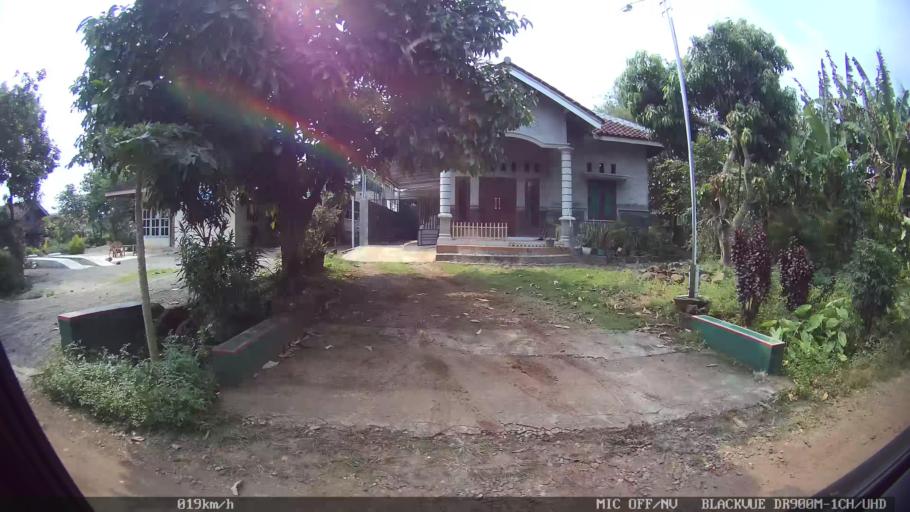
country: ID
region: Lampung
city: Gadingrejo
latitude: -5.3622
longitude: 105.0436
